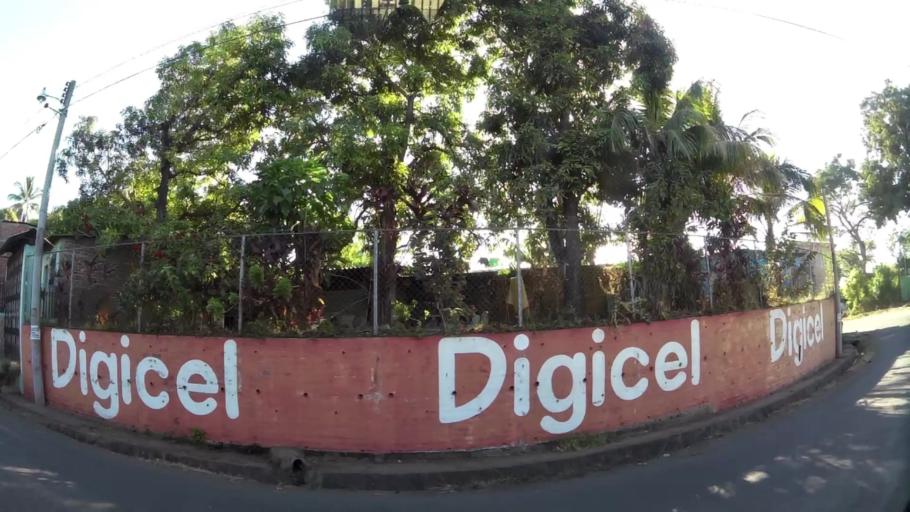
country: SV
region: Sonsonate
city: Sonsonate
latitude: 13.7071
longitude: -89.7167
